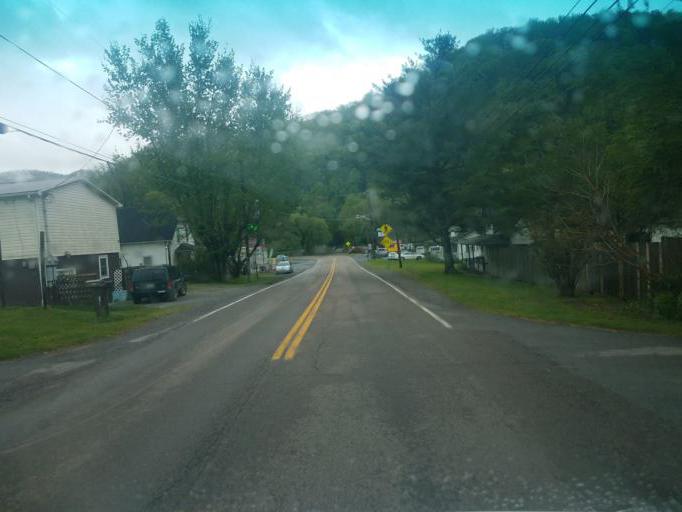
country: US
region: Virginia
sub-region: Washington County
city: Emory
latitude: 36.6319
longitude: -81.7834
